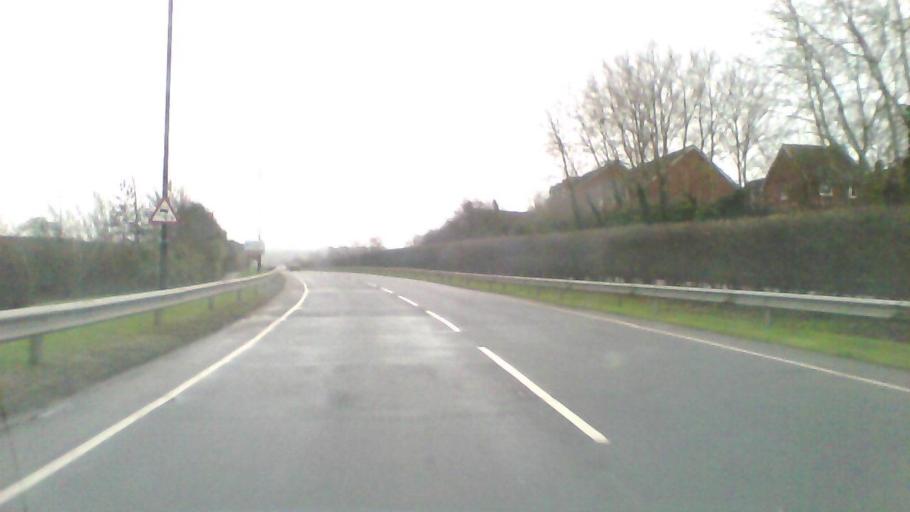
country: GB
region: England
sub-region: Isle of Wight
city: Newport
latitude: 50.7074
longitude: -1.2993
